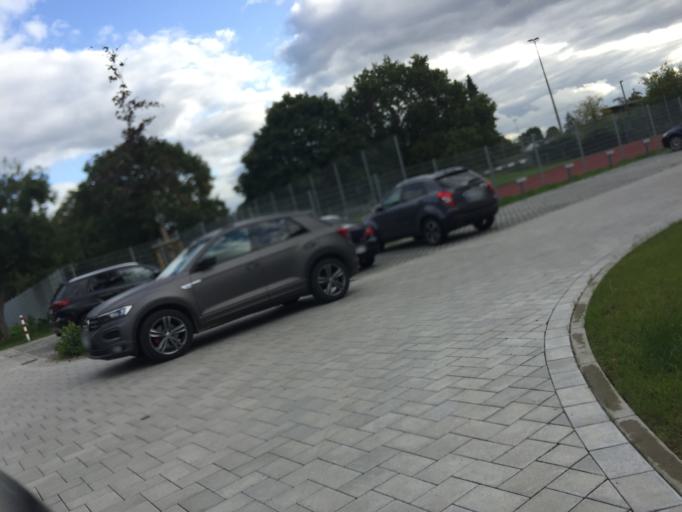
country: DE
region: Schleswig-Holstein
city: Itzehoe
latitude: 53.9366
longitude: 9.5050
